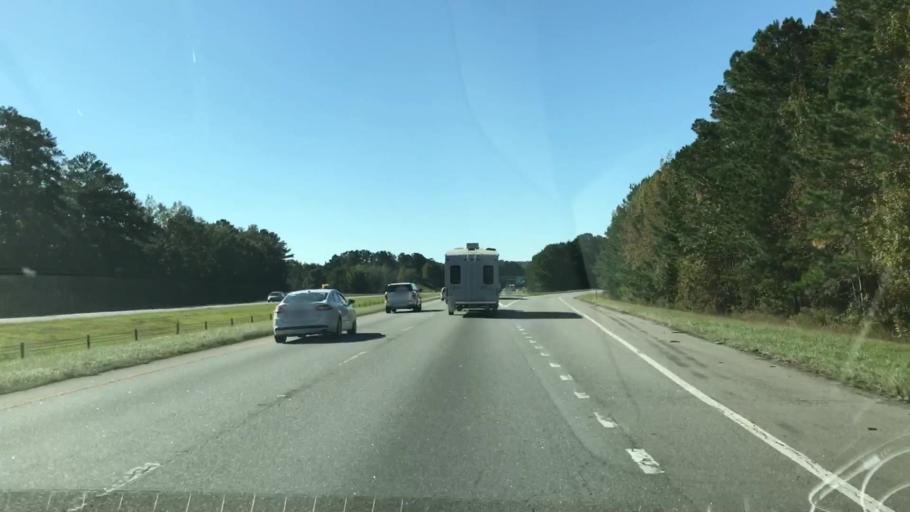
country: US
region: South Carolina
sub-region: Jasper County
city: Ridgeland
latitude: 32.5830
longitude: -80.9278
